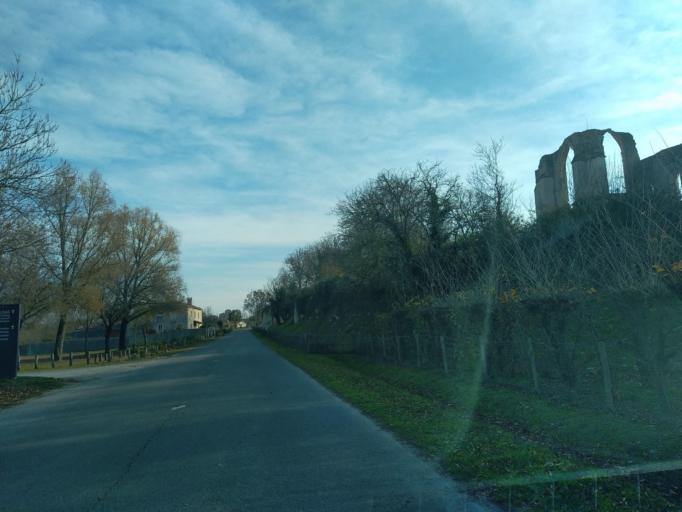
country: FR
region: Pays de la Loire
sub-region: Departement de la Vendee
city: Maillezais
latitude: 46.3742
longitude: -0.7474
